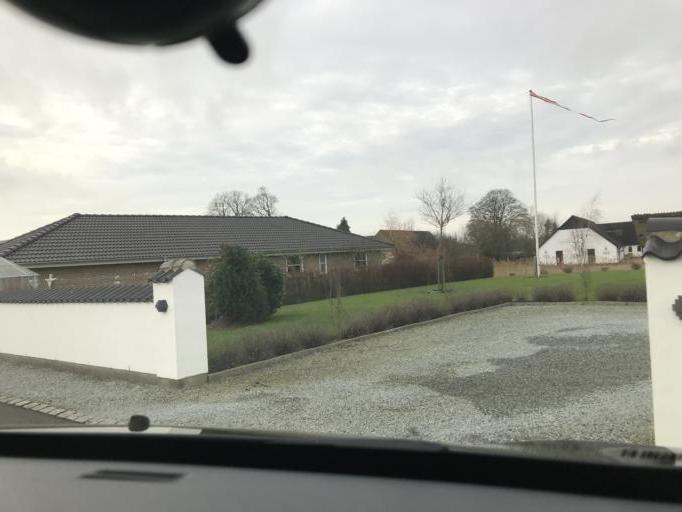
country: DK
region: South Denmark
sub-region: Faaborg-Midtfyn Kommune
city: Ringe
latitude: 55.2487
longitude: 10.4692
